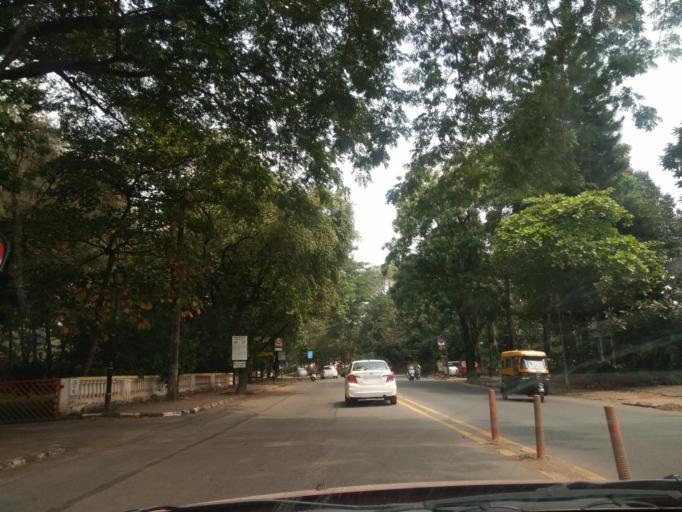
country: IN
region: Goa
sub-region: North Goa
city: Panaji
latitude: 15.4928
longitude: 73.8176
